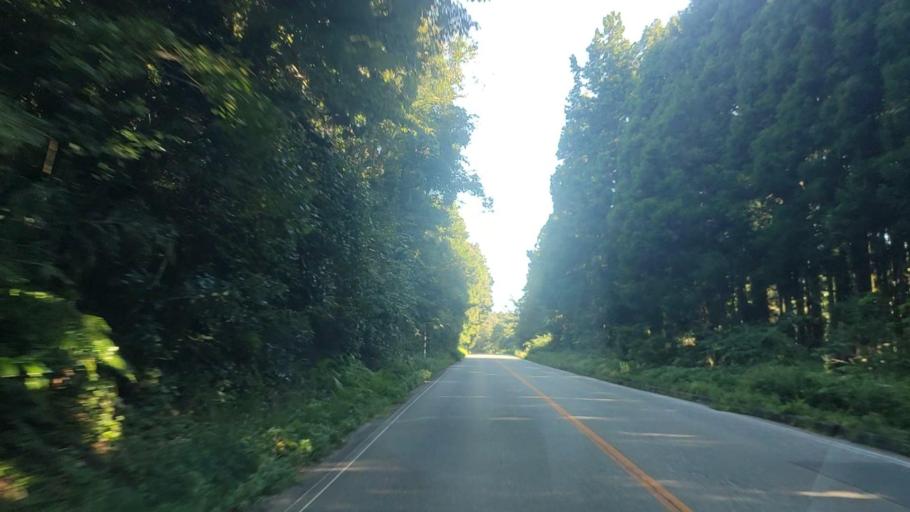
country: JP
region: Ishikawa
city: Nanao
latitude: 37.1042
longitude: 136.9476
